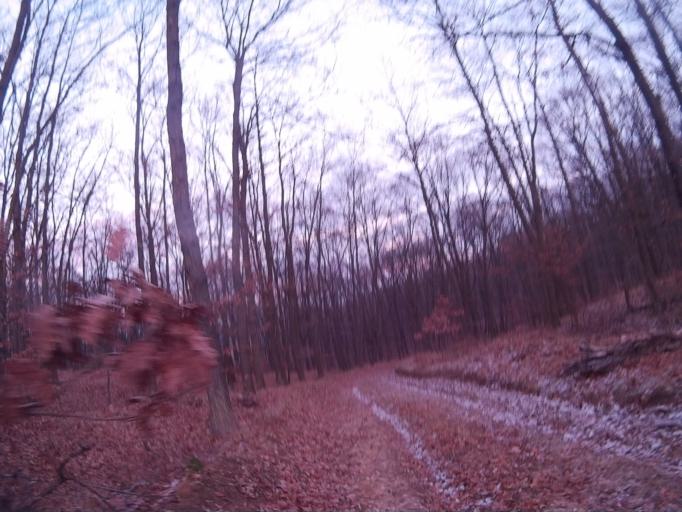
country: HU
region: Nograd
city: Rimoc
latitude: 47.9975
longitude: 19.4640
